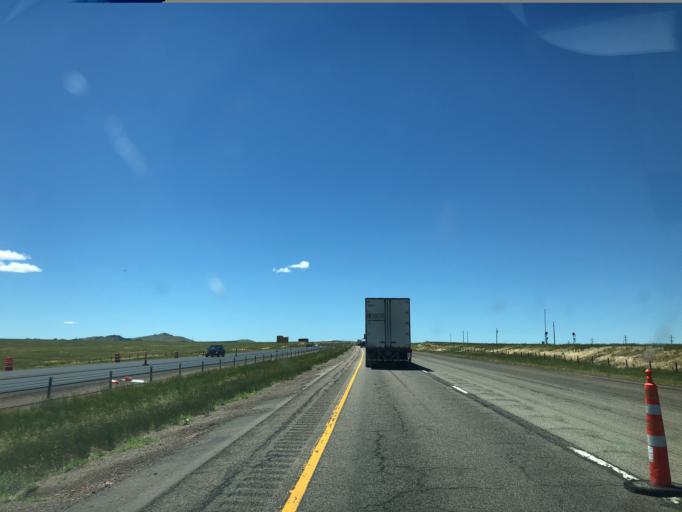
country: US
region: Wyoming
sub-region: Laramie County
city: Cheyenne
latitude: 41.0989
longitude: -105.1251
